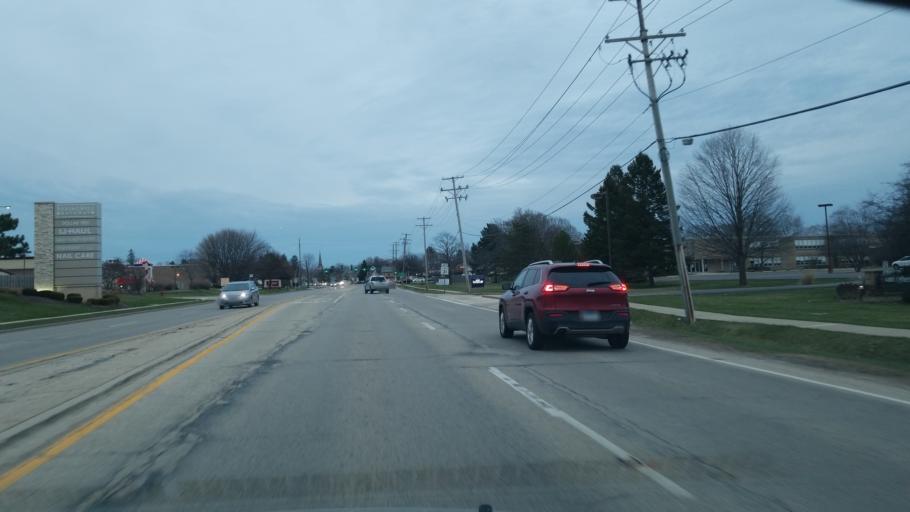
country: US
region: Illinois
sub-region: Kane County
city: West Dundee
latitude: 42.0985
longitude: -88.2906
